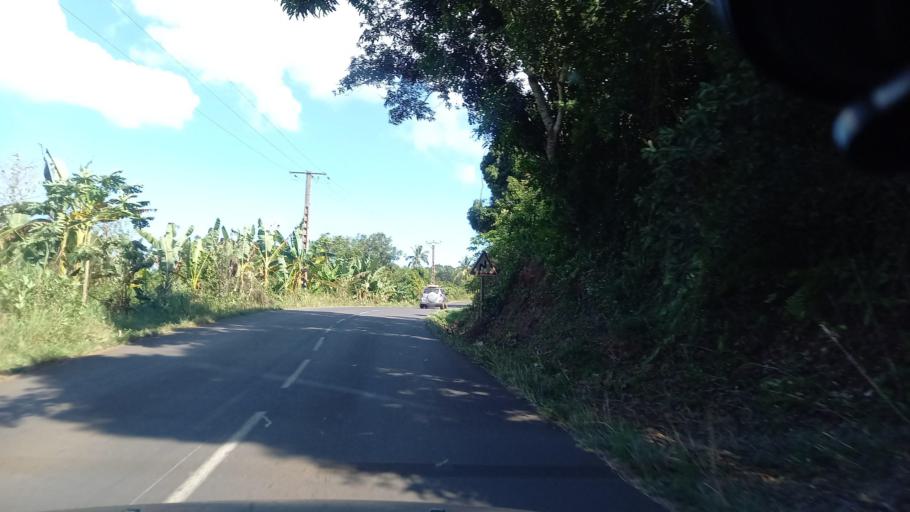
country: YT
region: M'Tsangamouji
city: M'Tsangamouji
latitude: -12.7628
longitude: 45.1007
